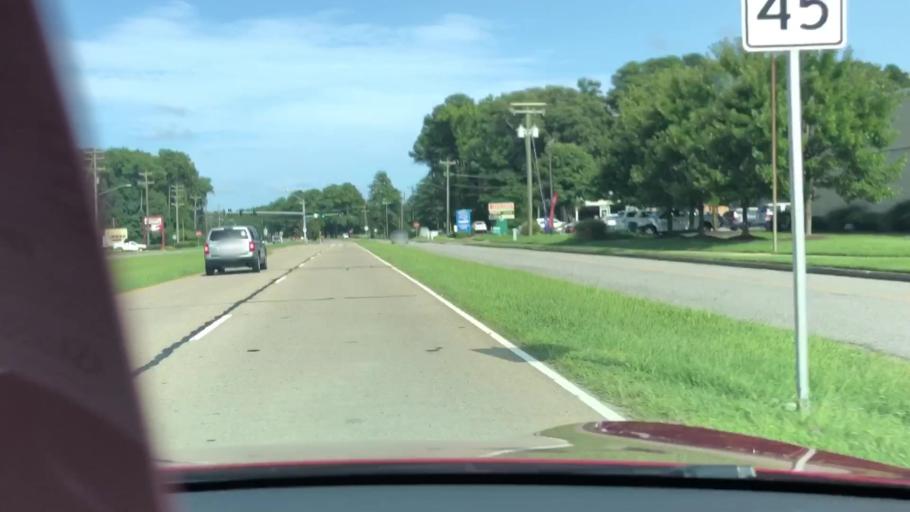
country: US
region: Virginia
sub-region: City of Virginia Beach
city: Virginia Beach
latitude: 36.8511
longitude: -76.0163
